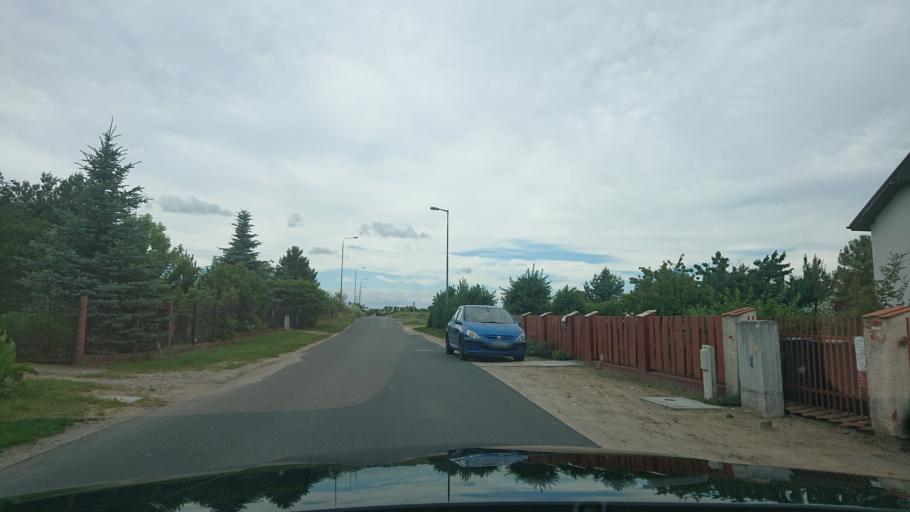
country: PL
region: Greater Poland Voivodeship
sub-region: Powiat gnieznienski
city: Gniezno
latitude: 52.5085
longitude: 17.6087
